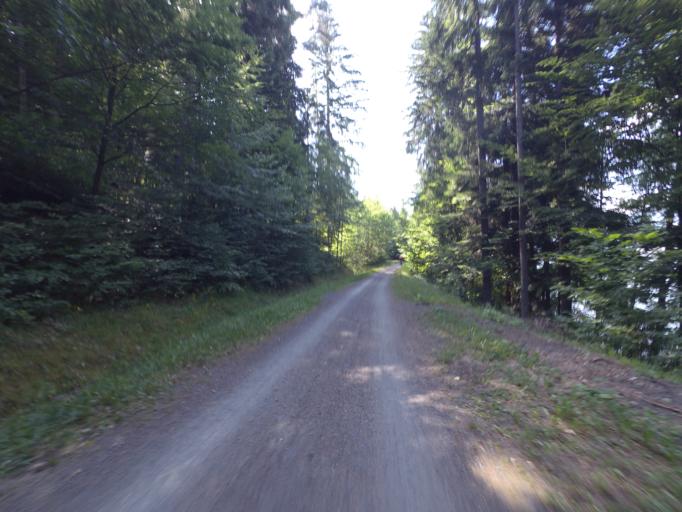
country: AT
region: Carinthia
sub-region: Politischer Bezirk Spittal an der Drau
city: Millstatt
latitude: 46.7878
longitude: 13.5861
